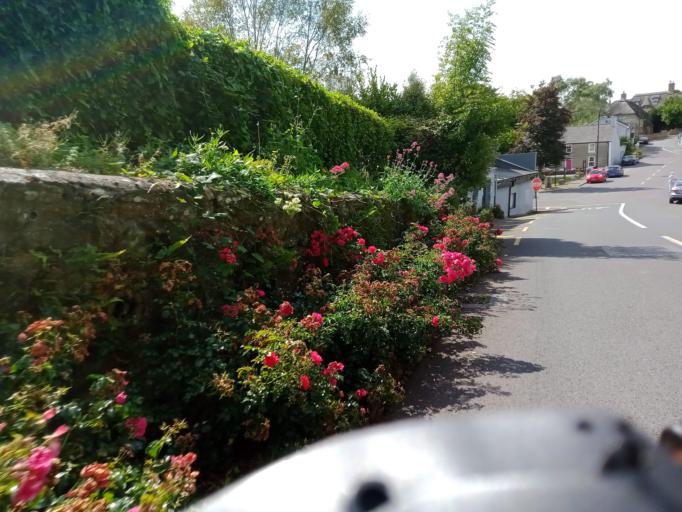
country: IE
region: Munster
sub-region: Waterford
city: Dungarvan
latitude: 52.1313
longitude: -7.4609
